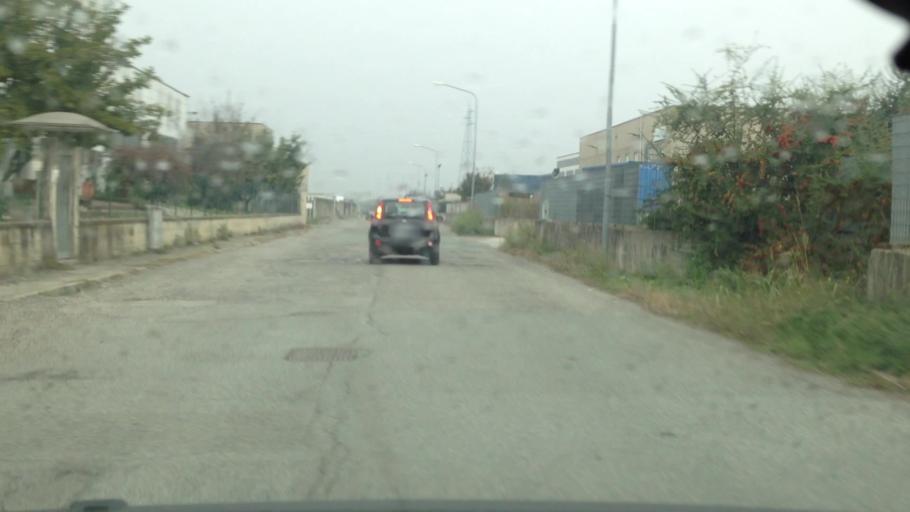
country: IT
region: Piedmont
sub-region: Provincia di Alessandria
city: Solero
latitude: 44.9153
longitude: 8.4827
